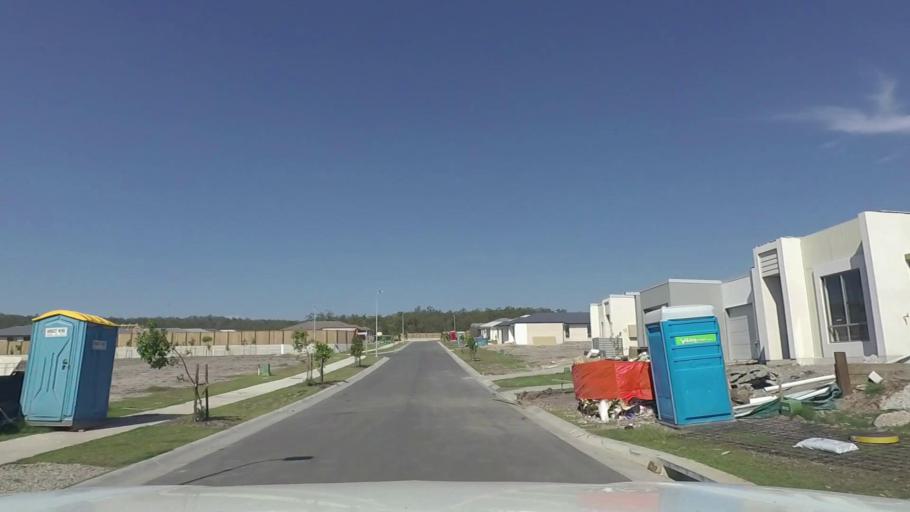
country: AU
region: Queensland
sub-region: Logan
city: Chambers Flat
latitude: -27.8157
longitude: 153.1281
